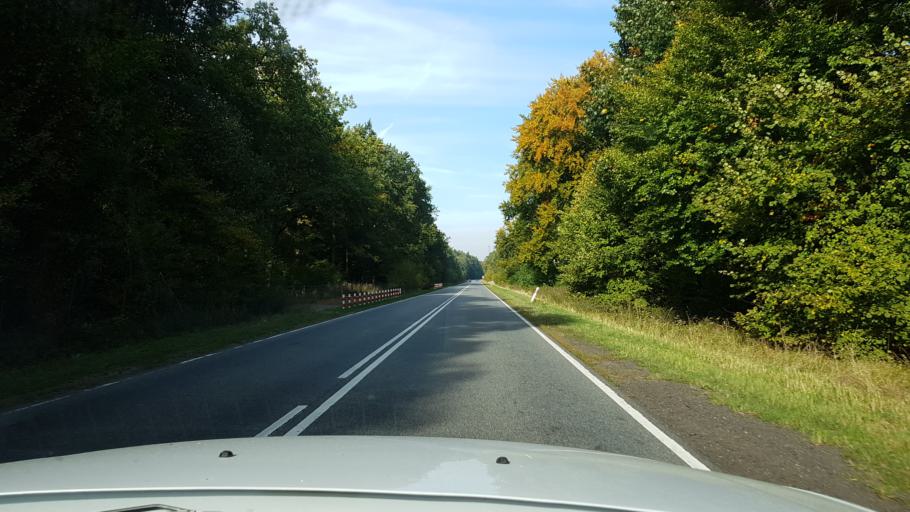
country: PL
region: West Pomeranian Voivodeship
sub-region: Powiat mysliborski
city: Nowogrodek Pomorski
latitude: 52.9243
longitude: 14.9602
